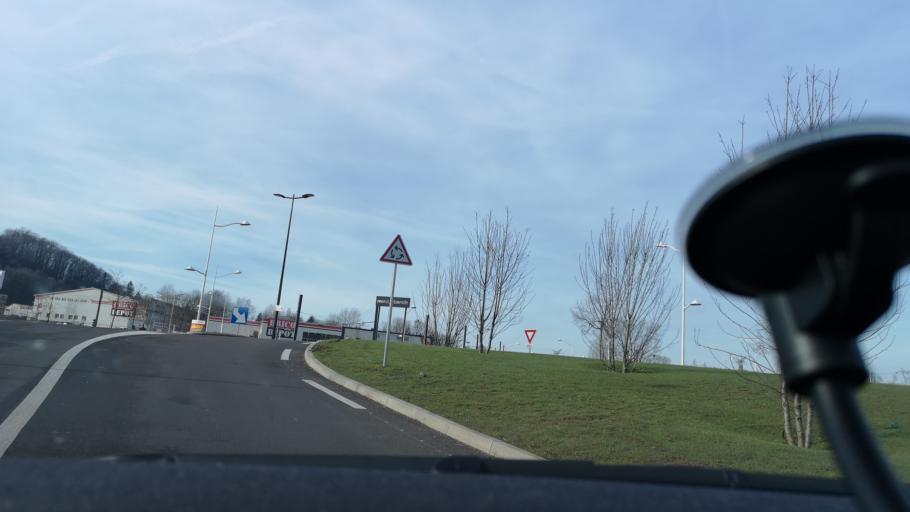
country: FR
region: Franche-Comte
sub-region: Departement du Doubs
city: Thise
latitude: 47.2626
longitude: 6.0621
